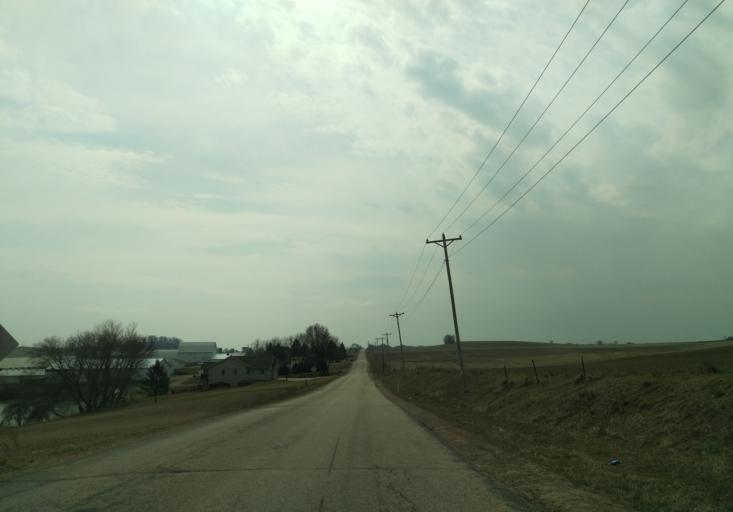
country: US
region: Wisconsin
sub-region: Dane County
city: Middleton
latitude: 43.1392
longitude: -89.4917
